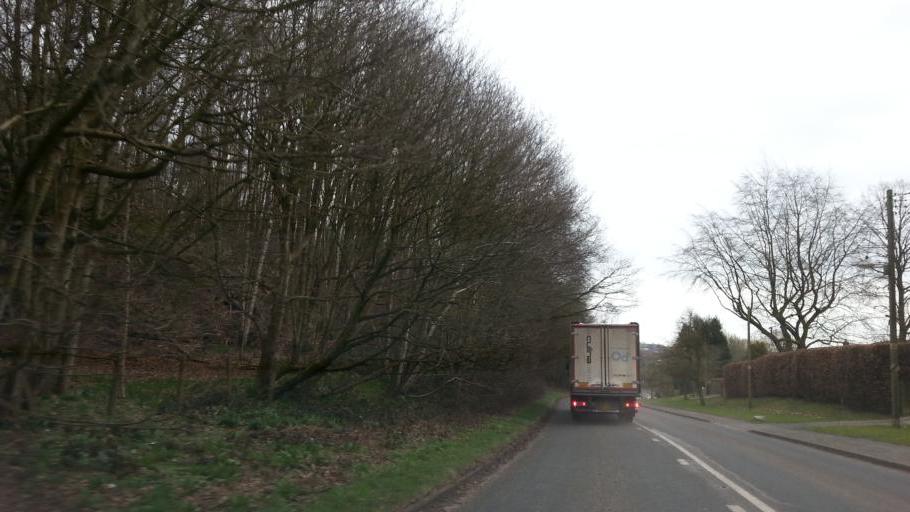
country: GB
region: England
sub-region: Staffordshire
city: Barlaston
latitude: 52.9186
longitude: -2.1770
